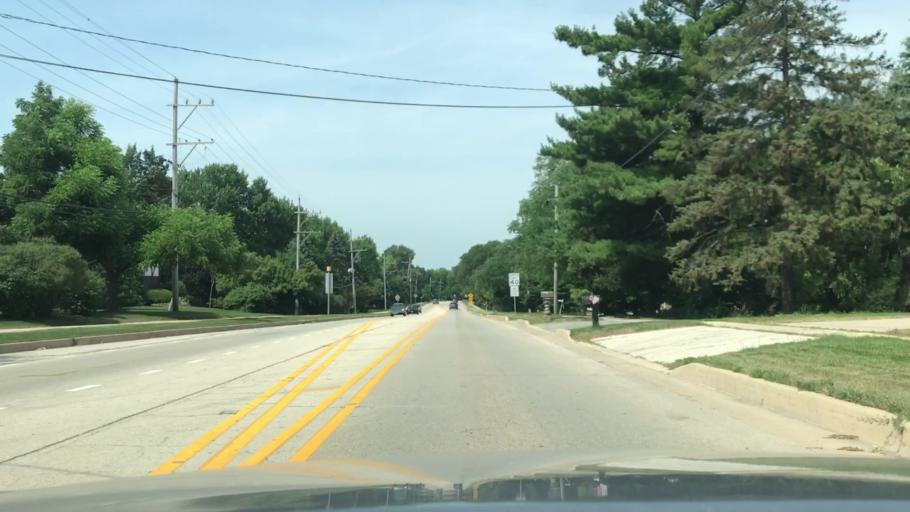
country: US
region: Illinois
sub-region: DuPage County
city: Darien
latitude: 41.7383
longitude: -88.0011
